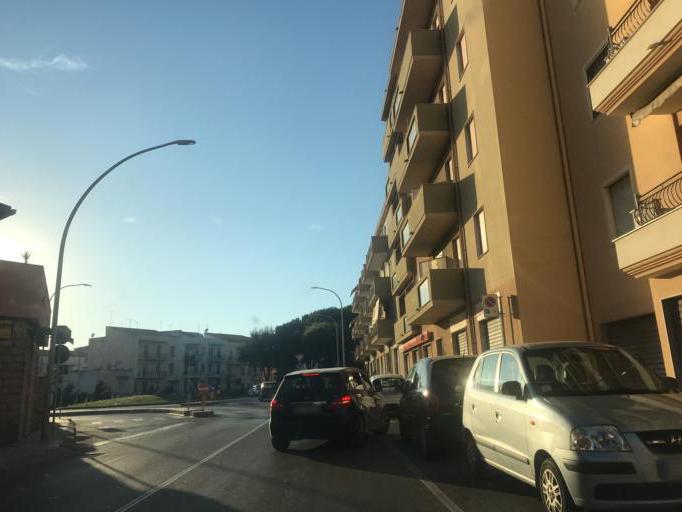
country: IT
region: Sardinia
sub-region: Provincia di Sassari
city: Alghero
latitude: 40.5724
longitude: 8.3231
